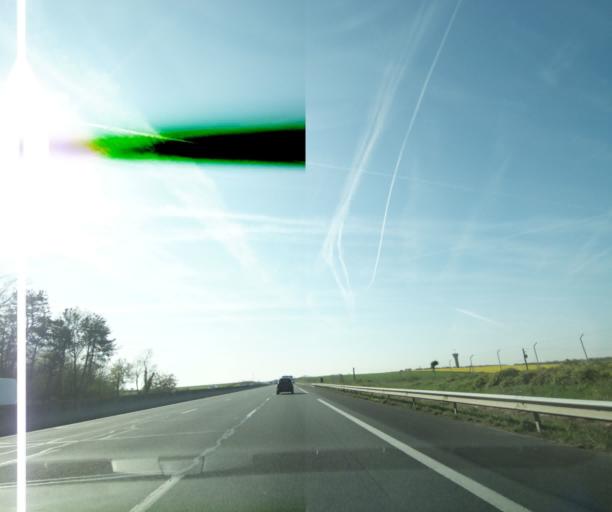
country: FR
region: Ile-de-France
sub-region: Departement de Seine-et-Marne
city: Bagneaux-sur-Loing
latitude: 48.2311
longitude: 2.7582
